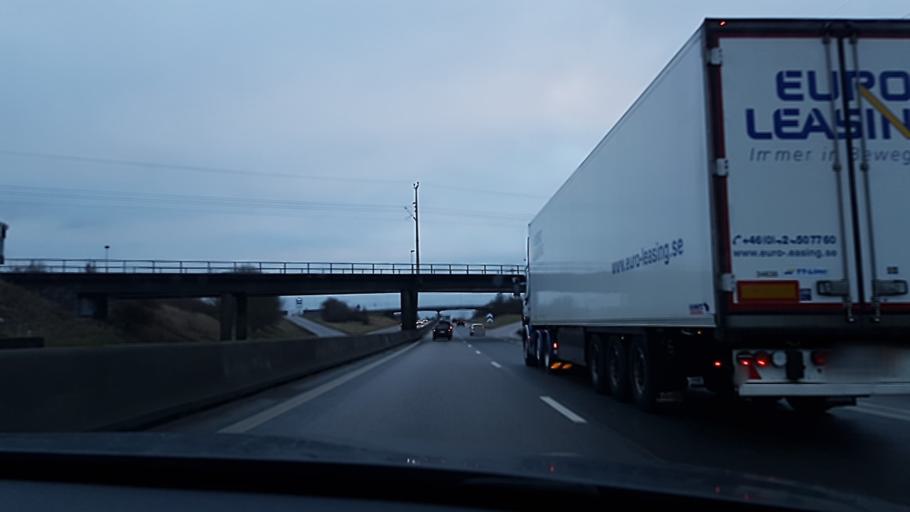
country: SE
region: Skane
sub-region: Astorps Kommun
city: Astorp
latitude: 56.1292
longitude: 12.9144
